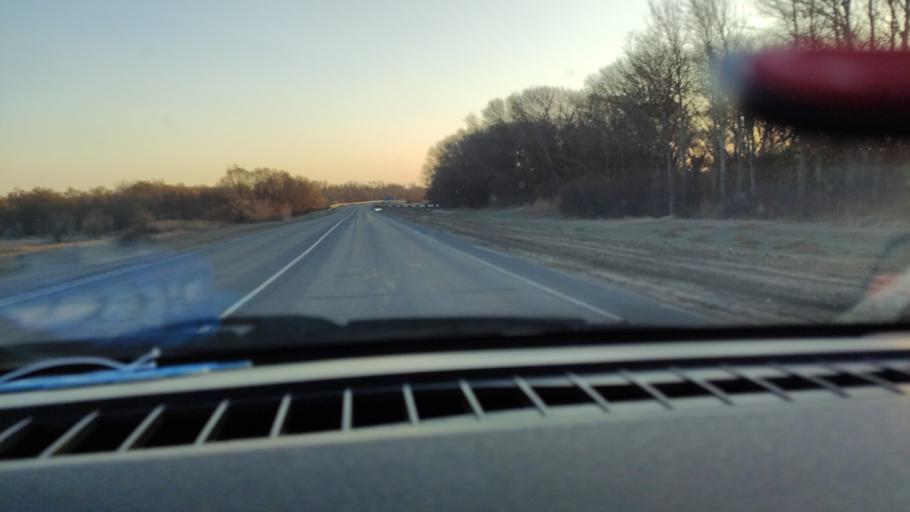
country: RU
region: Saratov
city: Sinodskoye
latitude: 51.9747
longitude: 46.6469
